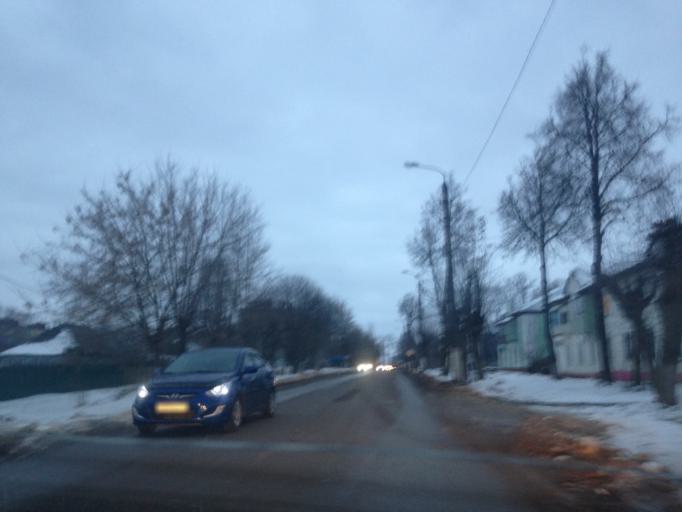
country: RU
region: Tula
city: Shchekino
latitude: 54.0008
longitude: 37.5271
